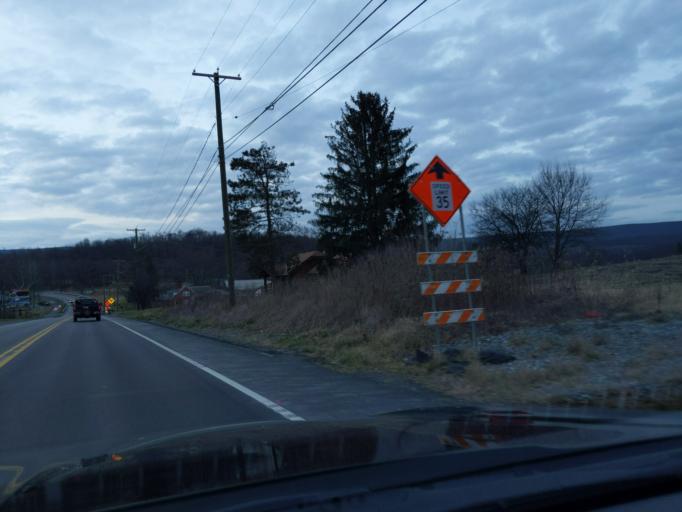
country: US
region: Pennsylvania
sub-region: Blair County
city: Williamsburg
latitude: 40.4745
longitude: -78.2711
